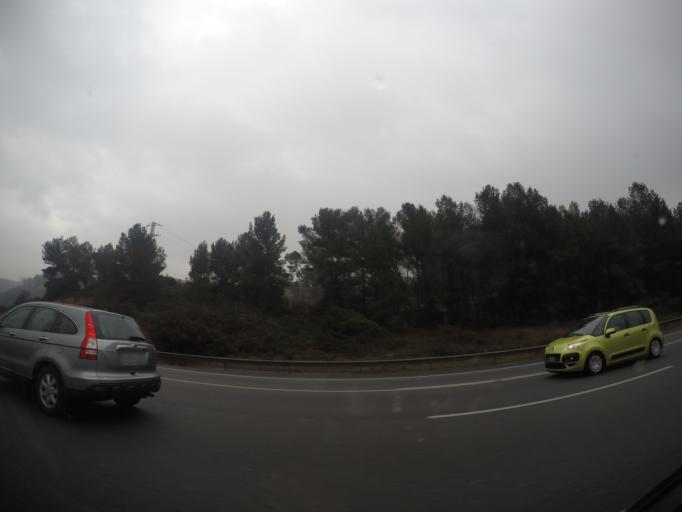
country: ES
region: Catalonia
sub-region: Provincia de Barcelona
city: Sant Andreu de la Barca
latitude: 41.4504
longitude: 1.9867
